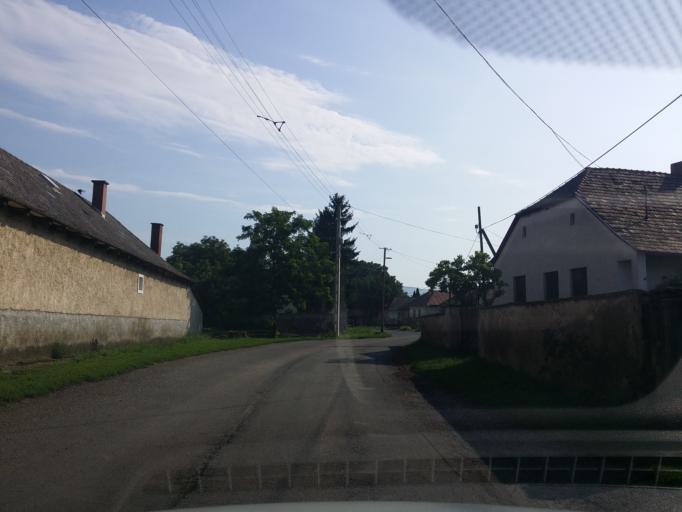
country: HU
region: Borsod-Abauj-Zemplen
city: Gonc
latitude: 48.3777
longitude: 21.2436
